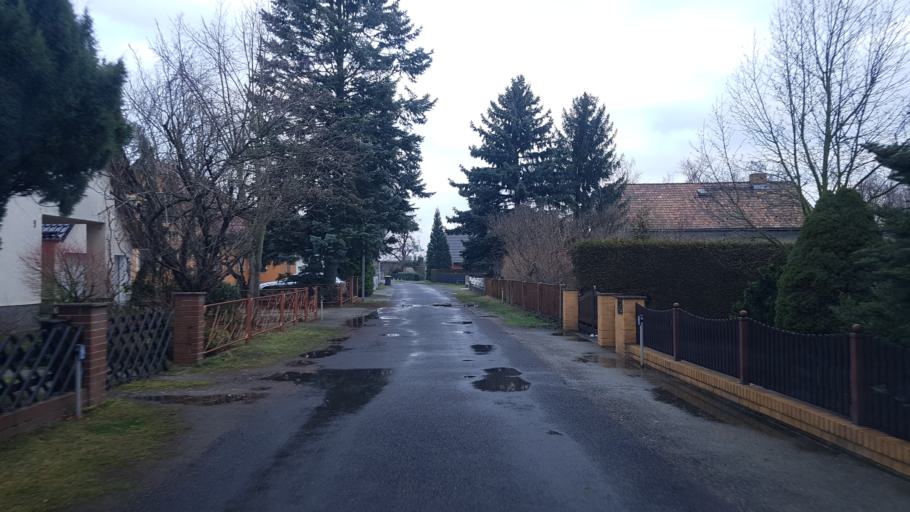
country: DE
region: Brandenburg
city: Elsterwerda
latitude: 51.4627
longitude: 13.5331
